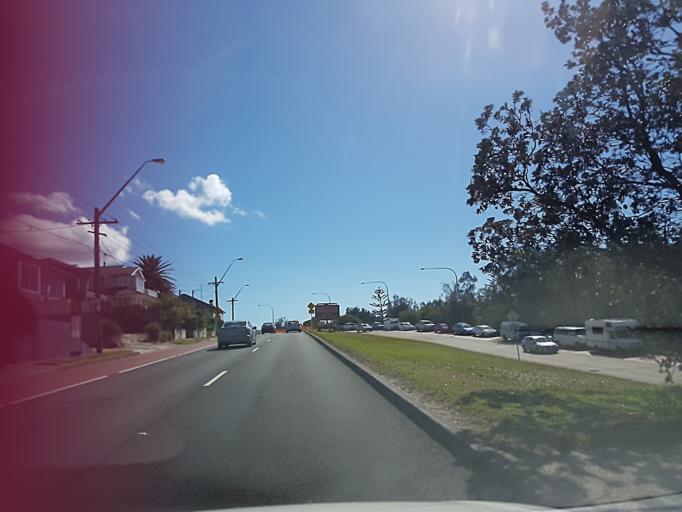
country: AU
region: New South Wales
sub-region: Warringah
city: Dee Why
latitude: -33.7439
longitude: 151.3029
